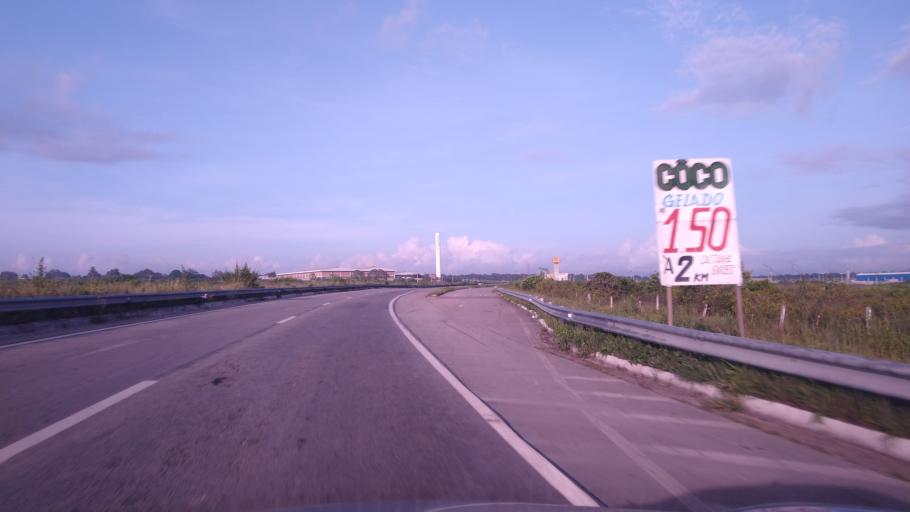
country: BR
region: Ceara
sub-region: Pacajus
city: Pacajus
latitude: -4.1611
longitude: -38.4844
